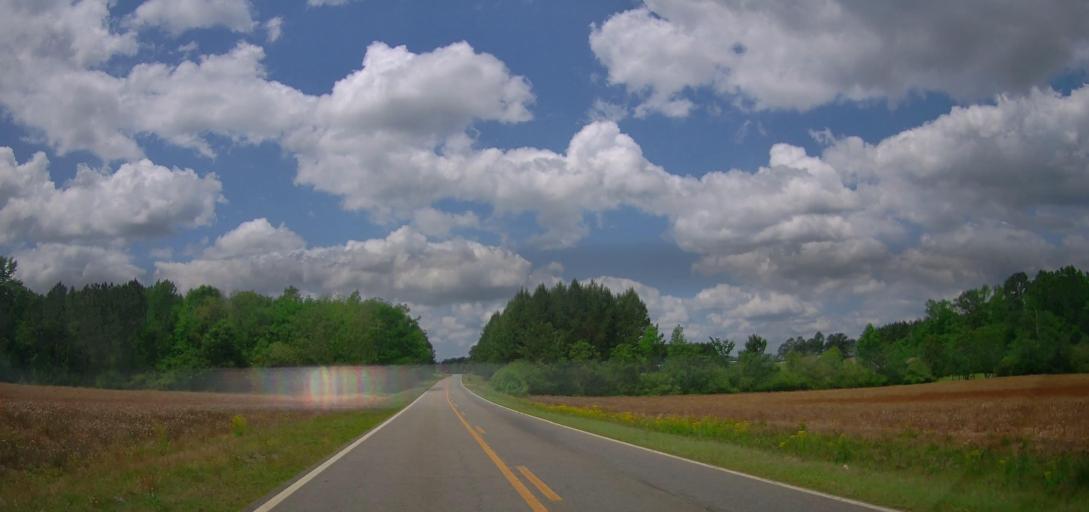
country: US
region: Georgia
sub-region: Laurens County
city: Dublin
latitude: 32.5996
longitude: -83.0026
